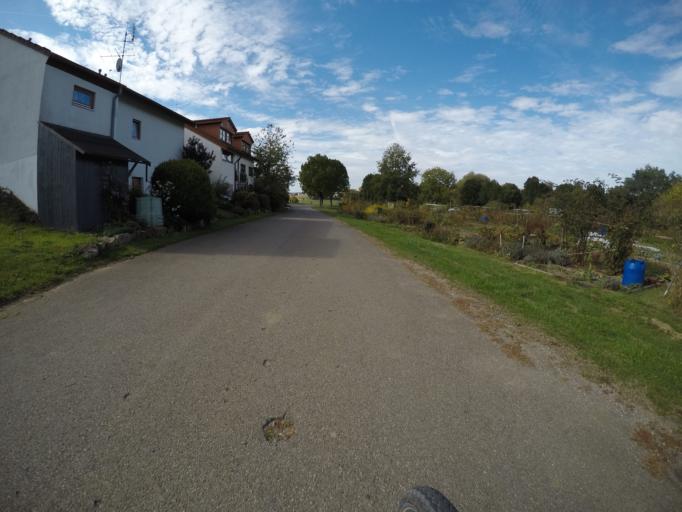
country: DE
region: Baden-Wuerttemberg
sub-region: Regierungsbezirk Stuttgart
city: Altdorf
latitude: 48.6299
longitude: 8.9899
